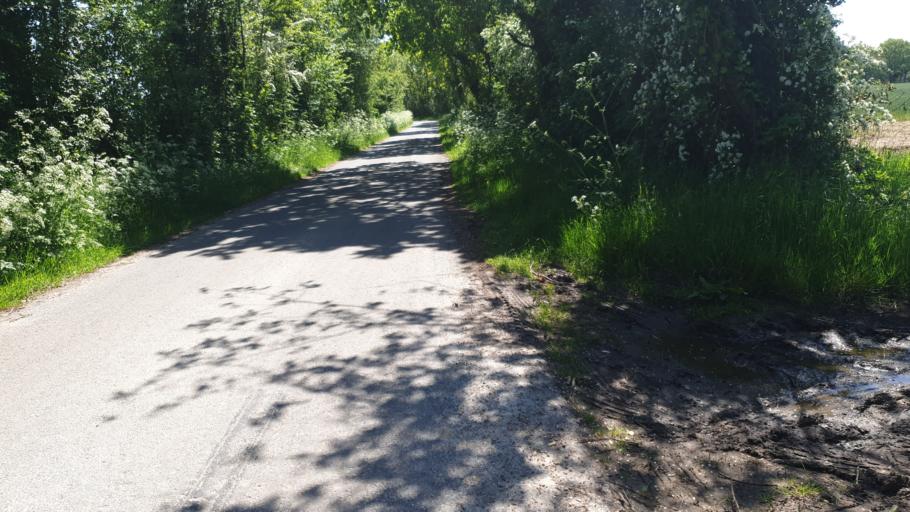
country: GB
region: England
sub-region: Essex
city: Great Bentley
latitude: 51.8915
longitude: 1.0380
